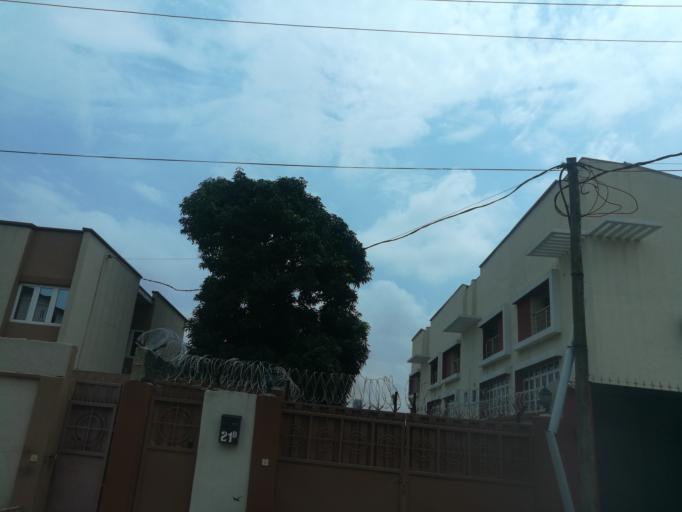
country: NG
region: Lagos
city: Ojota
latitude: 6.5906
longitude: 3.3654
